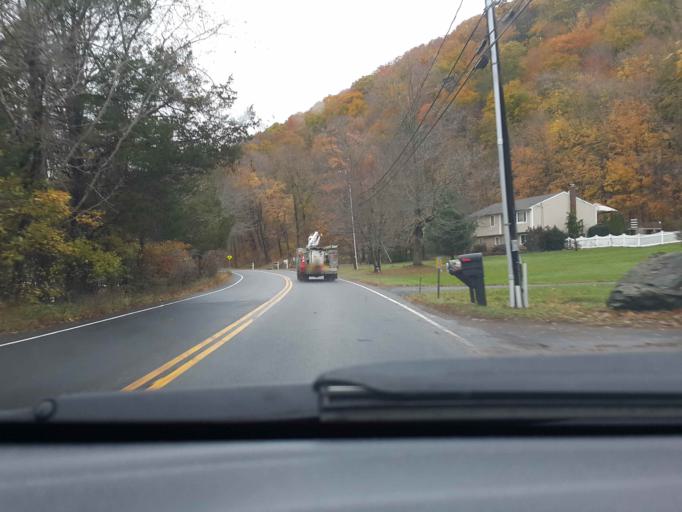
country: US
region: Connecticut
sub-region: Middlesex County
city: Durham
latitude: 41.4208
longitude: -72.6897
